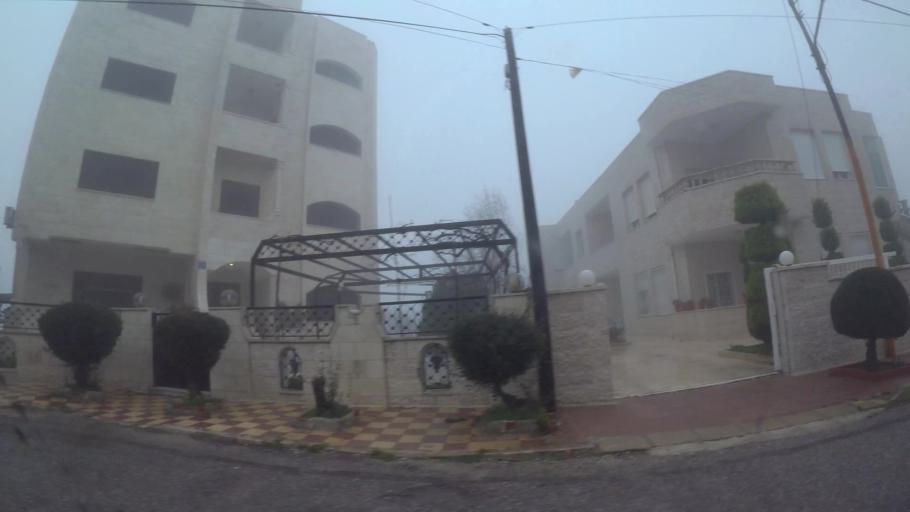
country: JO
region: Amman
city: Al Jubayhah
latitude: 32.0052
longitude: 35.8916
